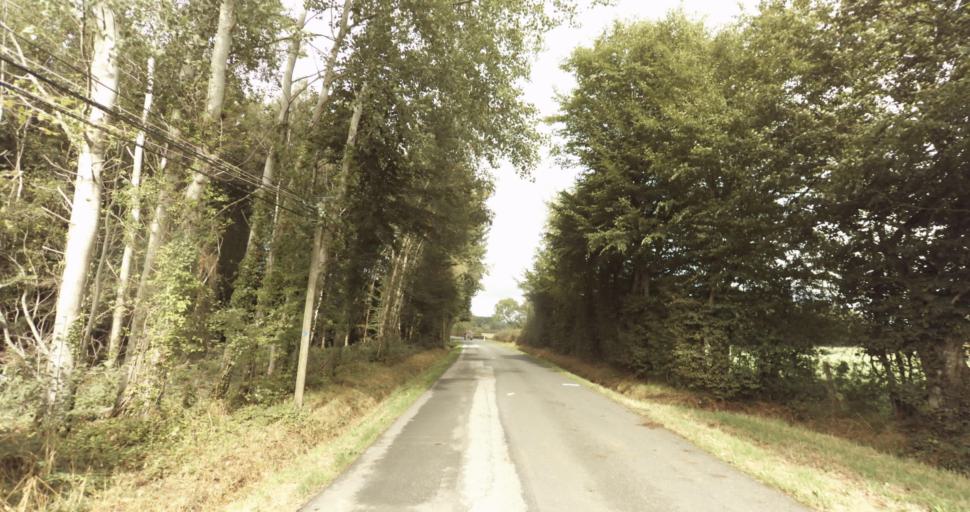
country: FR
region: Lower Normandy
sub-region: Departement de l'Orne
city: Gace
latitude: 48.8065
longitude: 0.2498
